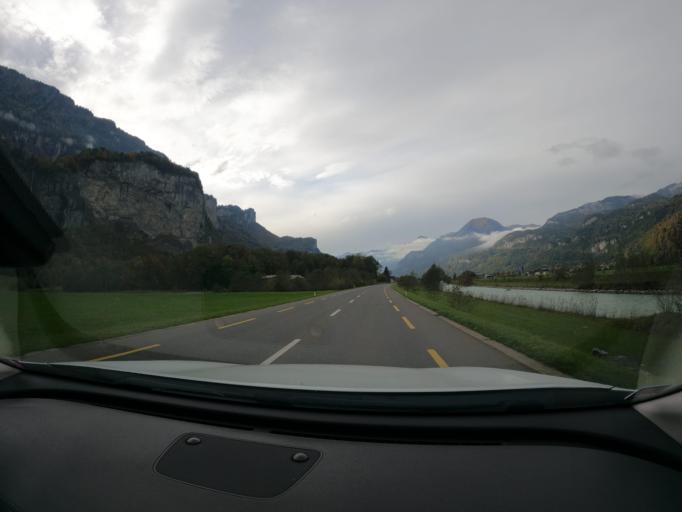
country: CH
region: Bern
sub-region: Interlaken-Oberhasli District
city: Meiringen
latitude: 46.7239
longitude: 8.1772
